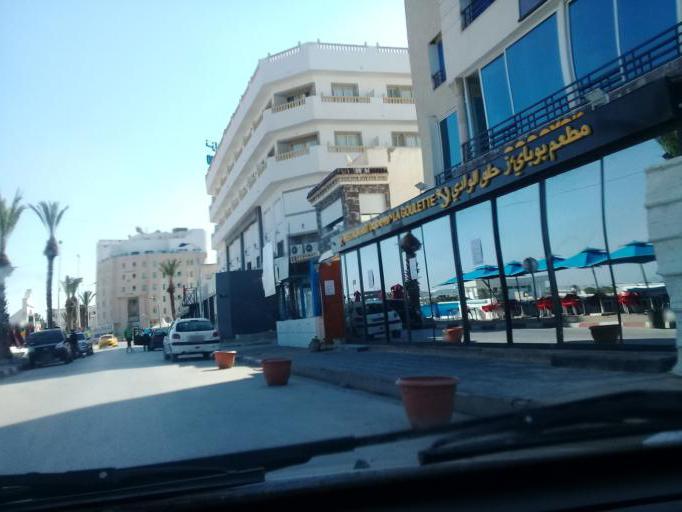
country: TN
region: Tunis
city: La Goulette
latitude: 36.8161
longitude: 10.3061
